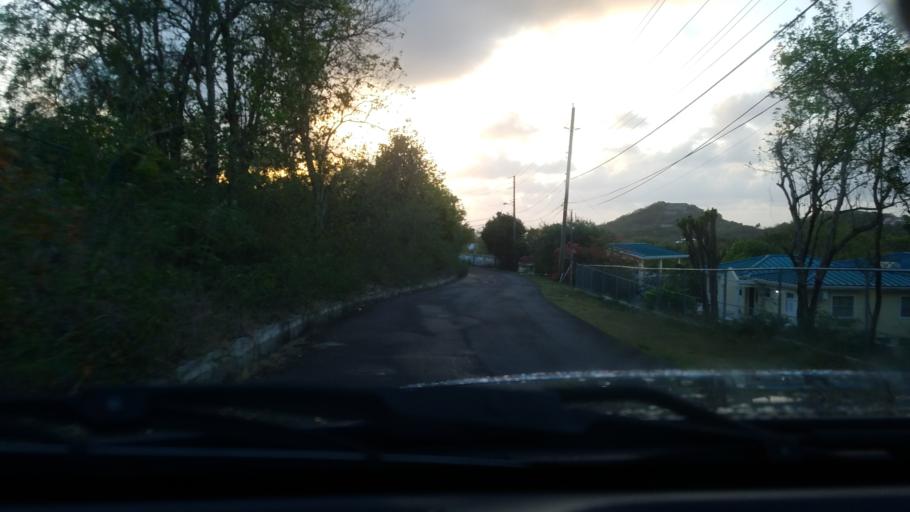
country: LC
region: Gros-Islet
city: Gros Islet
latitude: 14.0943
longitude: -60.9415
